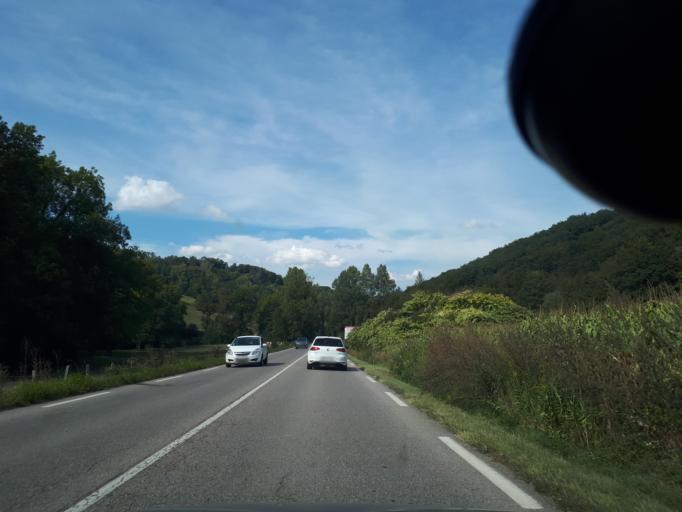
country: FR
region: Rhone-Alpes
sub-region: Departement de l'Isere
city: Maubec
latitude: 45.5575
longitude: 5.2748
